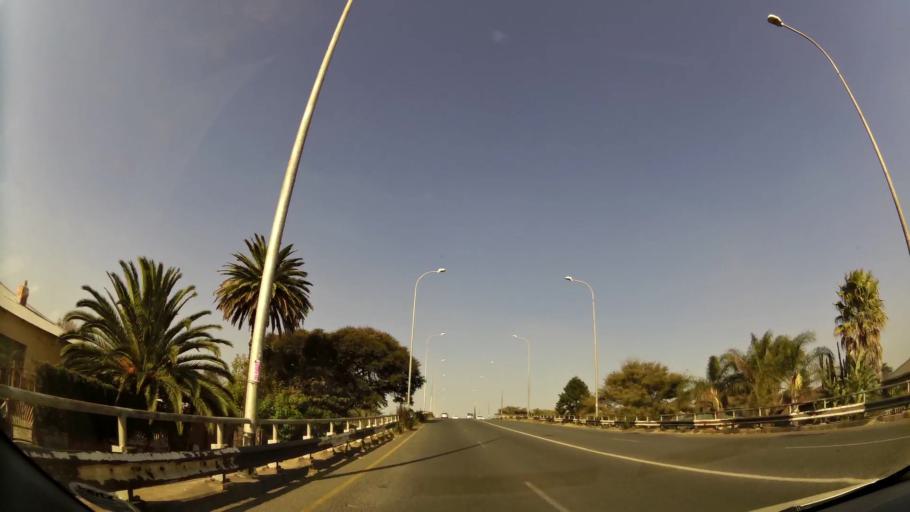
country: ZA
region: Gauteng
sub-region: West Rand District Municipality
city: Randfontein
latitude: -26.1716
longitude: 27.7035
